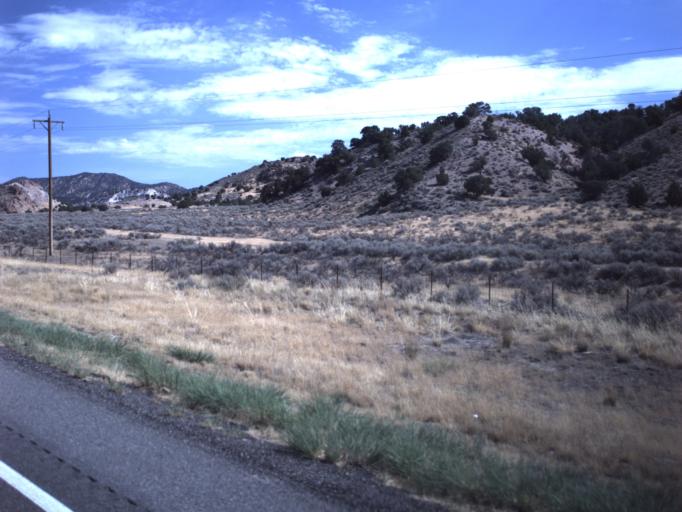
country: US
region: Utah
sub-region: Sanpete County
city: Gunnison
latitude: 39.3570
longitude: -111.9296
